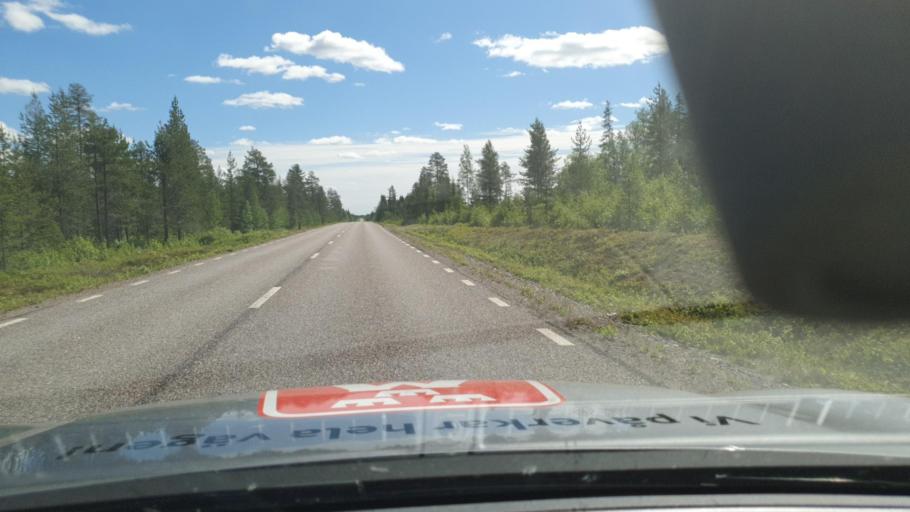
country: SE
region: Norrbotten
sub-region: Pajala Kommun
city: Pajala
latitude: 67.1516
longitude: 23.5584
